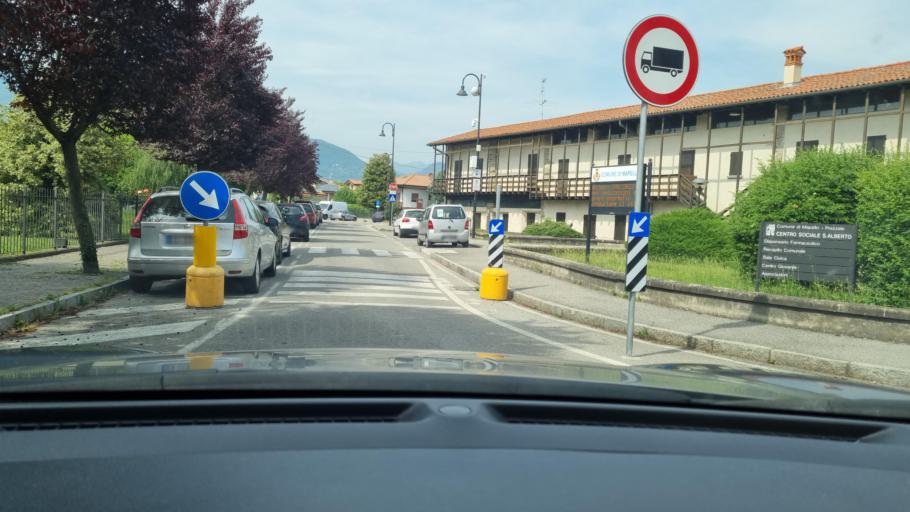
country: IT
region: Lombardy
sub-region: Provincia di Bergamo
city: Mapello
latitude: 45.7188
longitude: 9.5607
